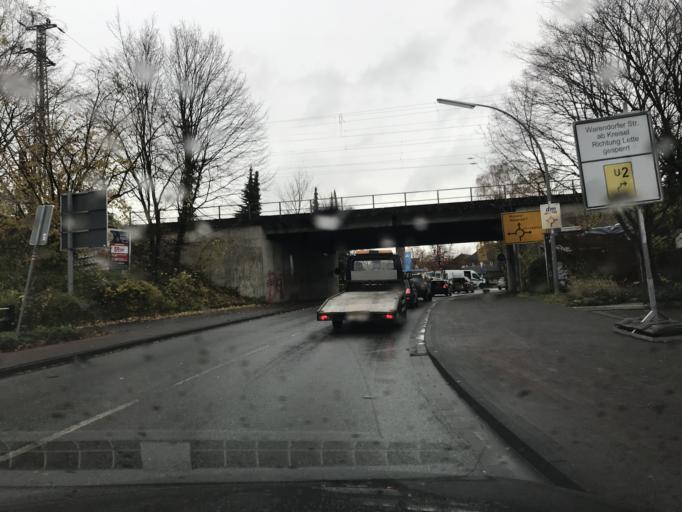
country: DE
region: North Rhine-Westphalia
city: Oelde
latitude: 51.8299
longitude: 8.1513
